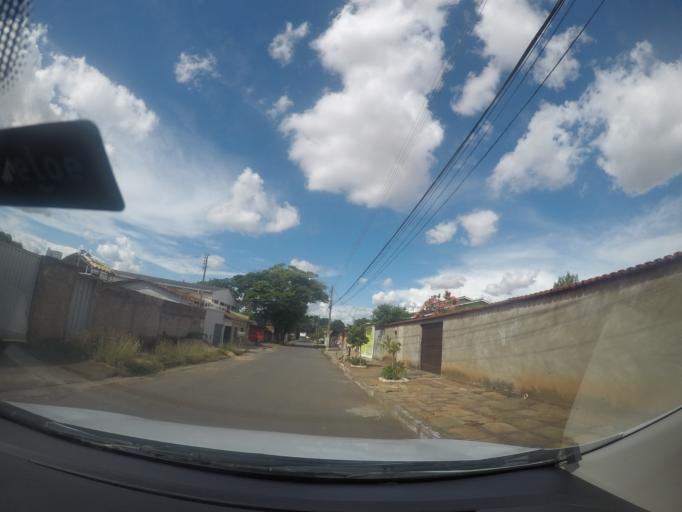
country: BR
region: Goias
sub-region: Goiania
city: Goiania
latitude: -16.6757
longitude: -49.3007
